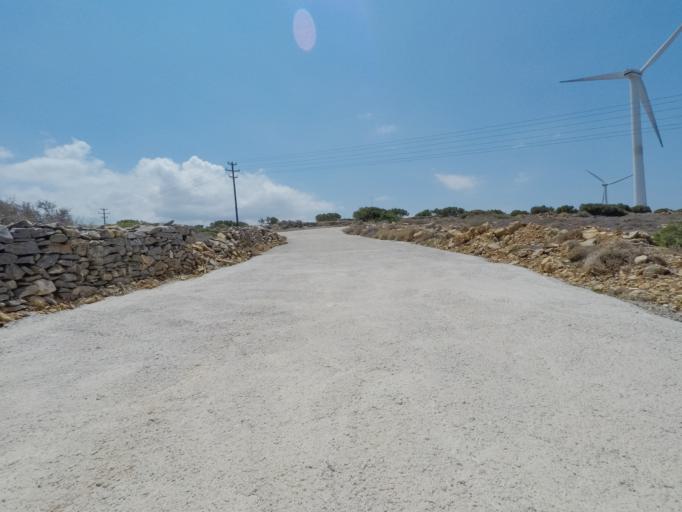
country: GR
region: Crete
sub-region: Nomos Lasithiou
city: Elounda
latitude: 35.3228
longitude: 25.7541
